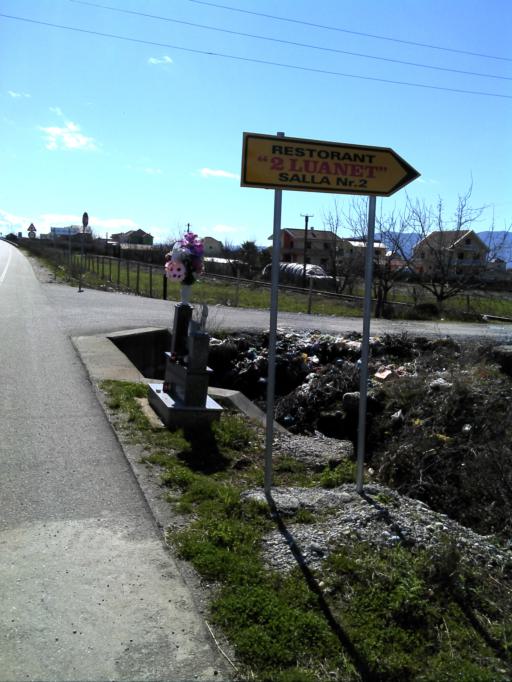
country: AL
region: Shkoder
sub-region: Rrethi i Malesia e Madhe
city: Grude-Fushe
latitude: 42.1576
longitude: 19.4726
